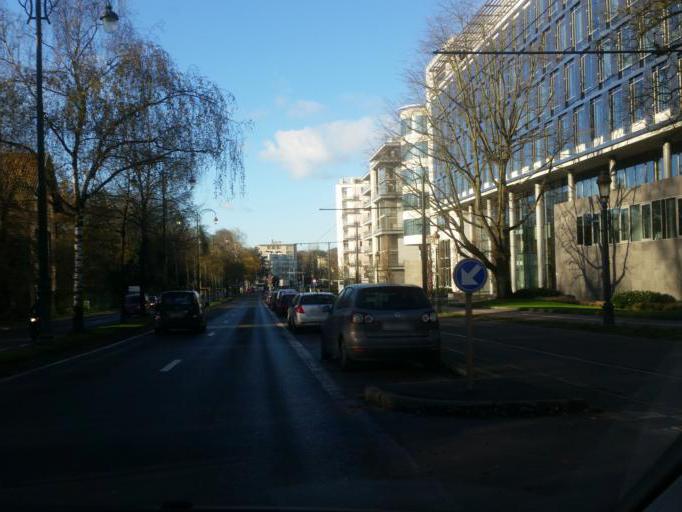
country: BE
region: Flanders
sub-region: Provincie Vlaams-Brabant
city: Sint-Genesius-Rode
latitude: 50.7965
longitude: 4.4001
